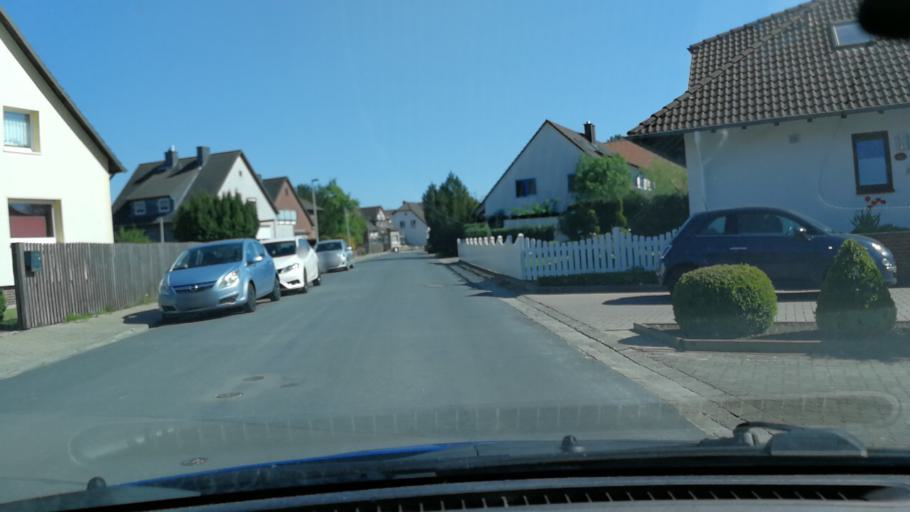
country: DE
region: Lower Saxony
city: Lehrte
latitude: 52.3673
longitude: 9.9101
